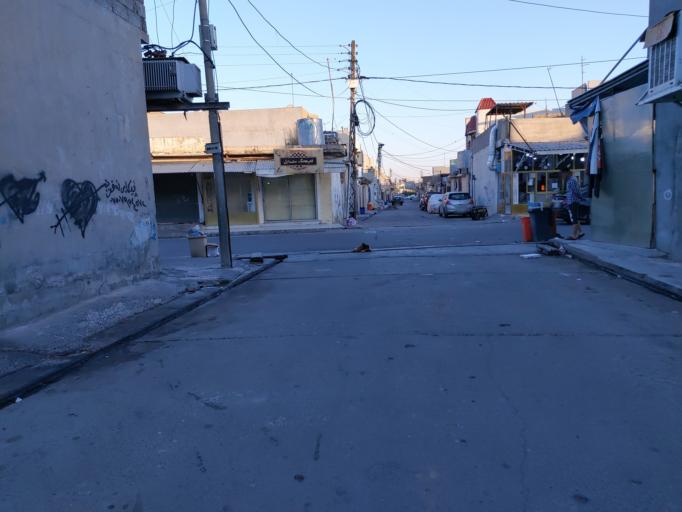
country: IQ
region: Arbil
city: Erbil
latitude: 36.1600
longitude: 43.9904
